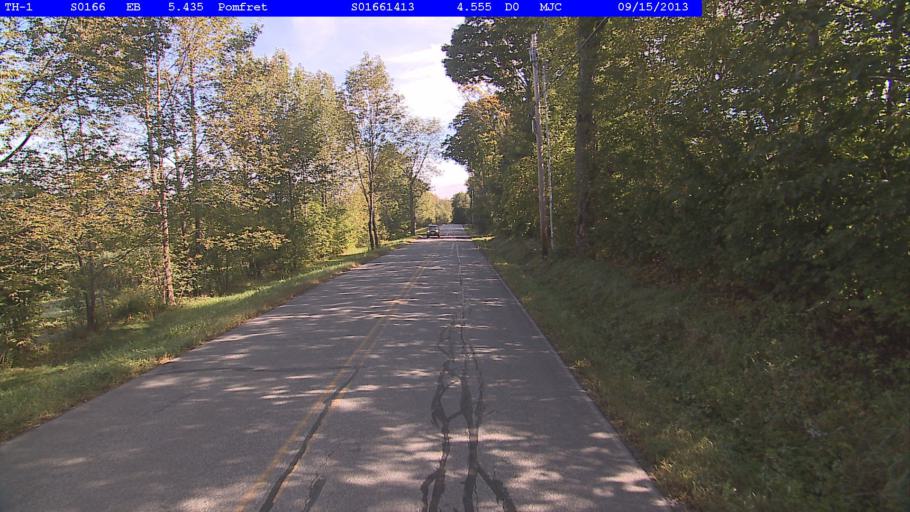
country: US
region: Vermont
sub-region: Windsor County
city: Woodstock
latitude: 43.7076
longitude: -72.5125
